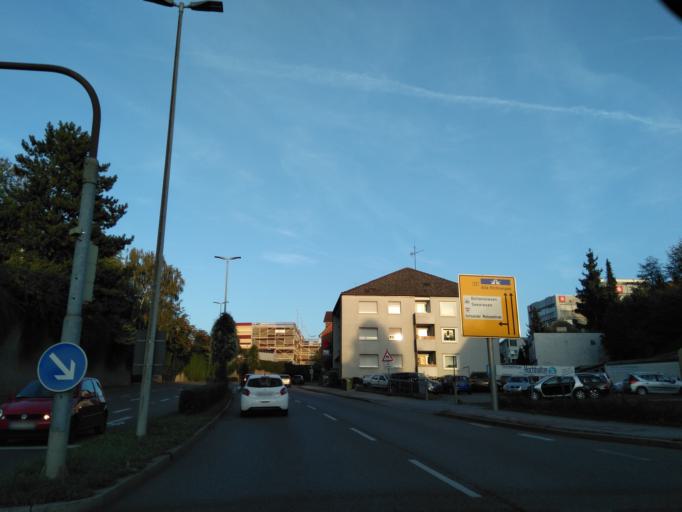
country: DE
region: Baden-Wuerttemberg
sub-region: Regierungsbezirk Stuttgart
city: Bietigheim-Bissingen
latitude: 48.9563
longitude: 9.1332
